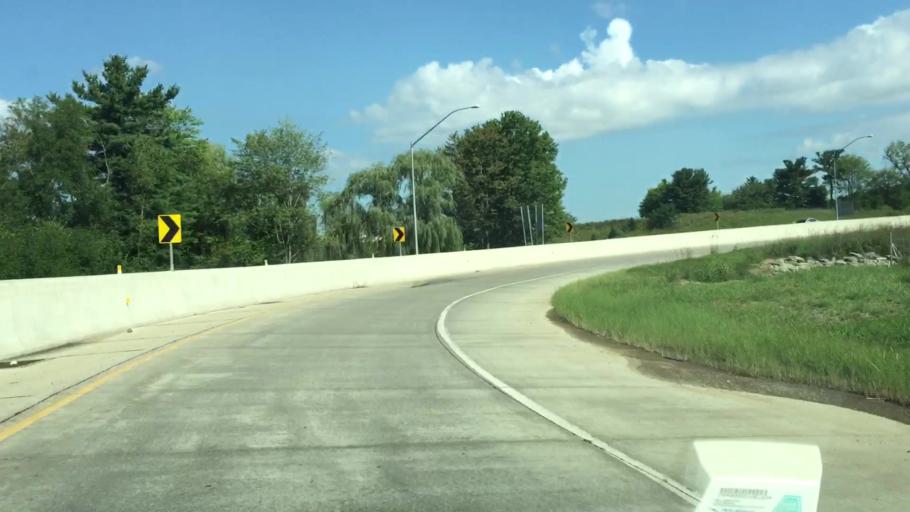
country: US
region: Pennsylvania
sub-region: Butler County
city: Cranberry Township
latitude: 40.6871
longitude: -80.0981
